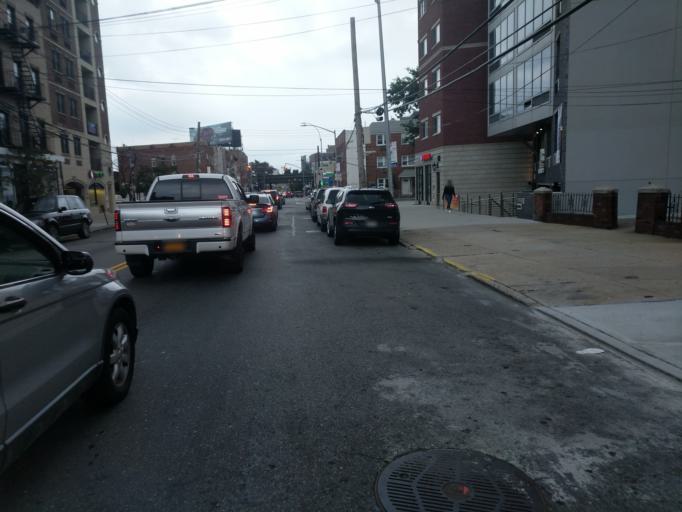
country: US
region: New York
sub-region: Queens County
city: Long Island City
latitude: 40.7706
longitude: -73.9205
